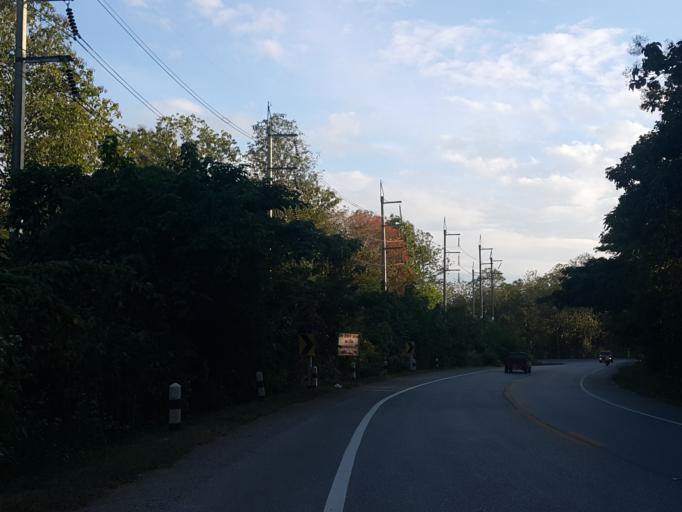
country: TH
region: Lampang
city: Lampang
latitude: 18.4827
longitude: 99.5489
